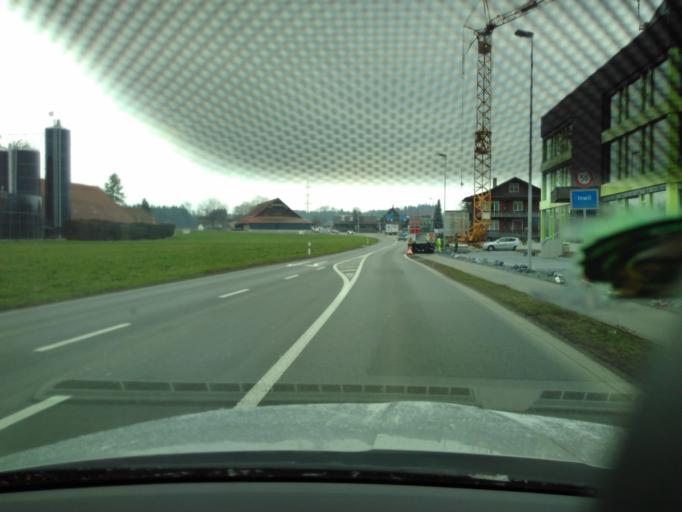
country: CH
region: Lucerne
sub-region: Hochdorf District
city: Inwil
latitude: 47.1198
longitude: 8.3417
